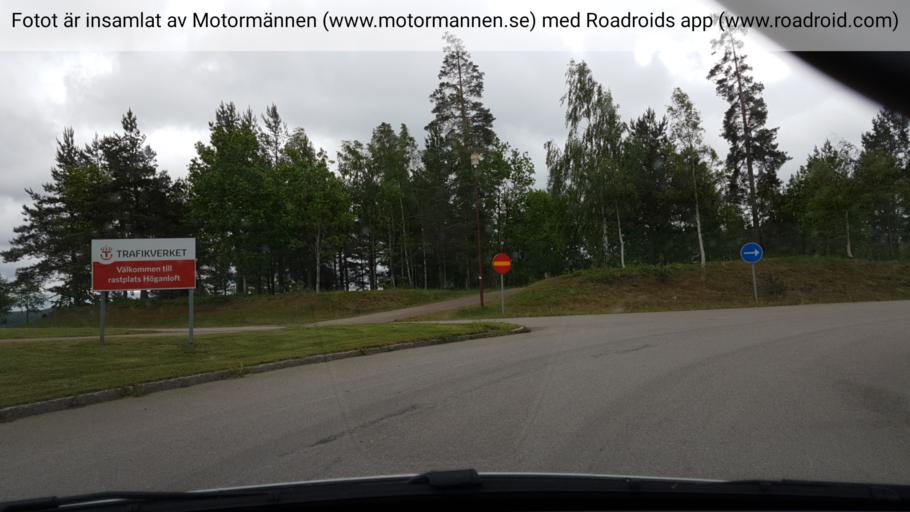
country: SE
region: Joenkoeping
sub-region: Tranas Kommun
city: Tranas
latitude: 58.0323
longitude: 14.9520
